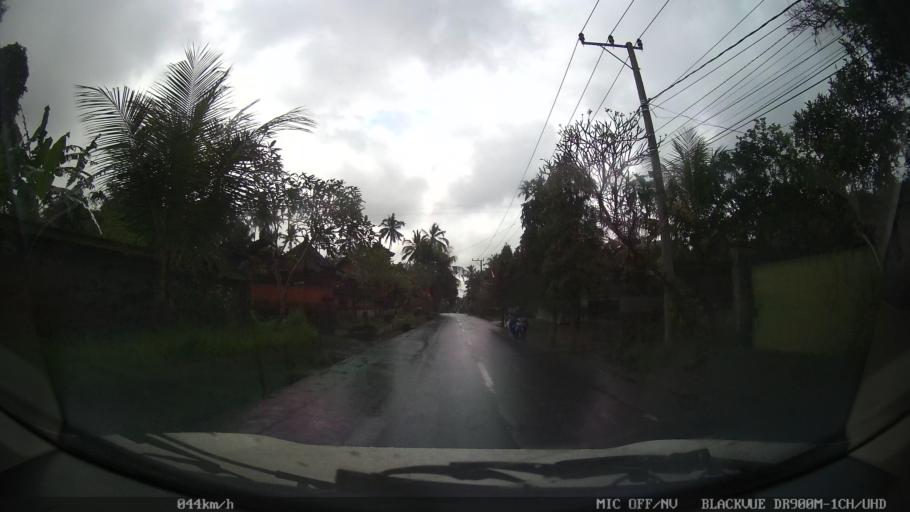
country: ID
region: Bali
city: Banjar Tengah
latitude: -8.5013
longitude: 115.1880
